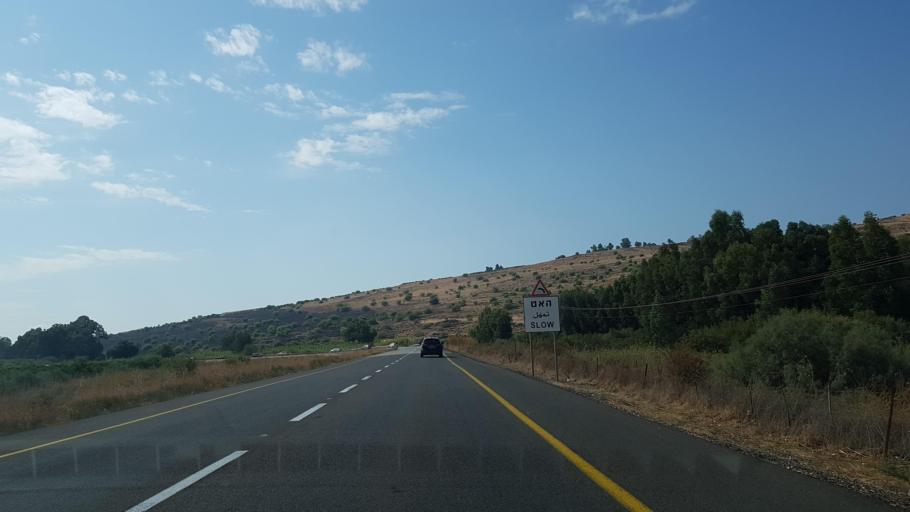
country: SY
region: Quneitra
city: Al Butayhah
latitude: 32.9045
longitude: 35.6207
